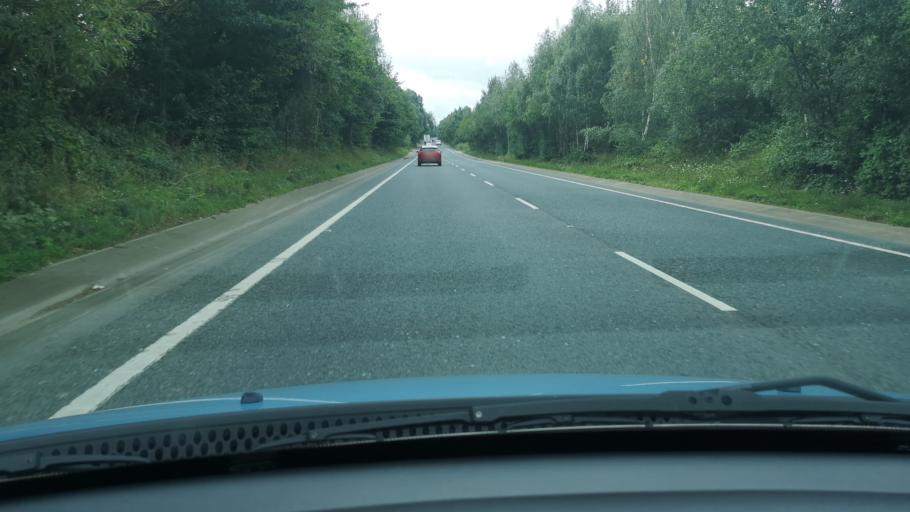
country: GB
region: England
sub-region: City and Borough of Wakefield
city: Hemsworth
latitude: 53.6028
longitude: -1.3565
